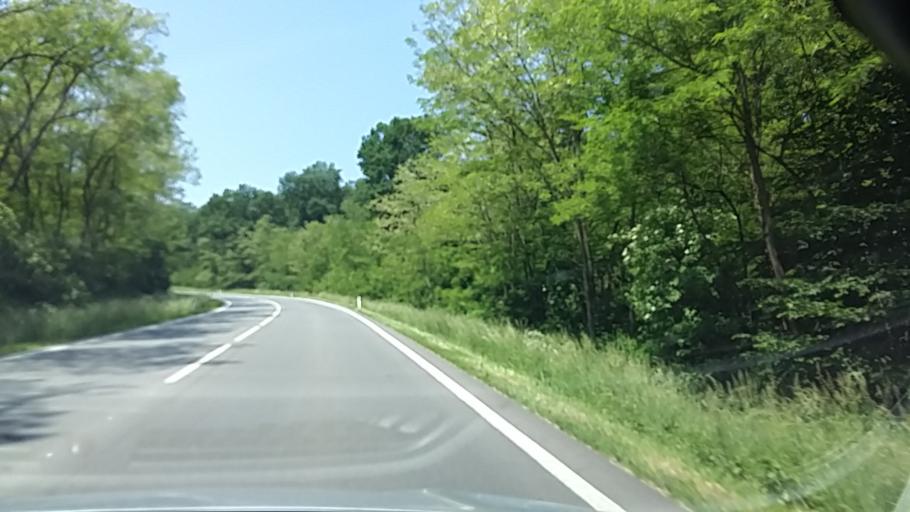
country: AT
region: Burgenland
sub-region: Politischer Bezirk Oberpullendorf
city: Oberpullendorf
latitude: 47.5267
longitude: 16.5160
